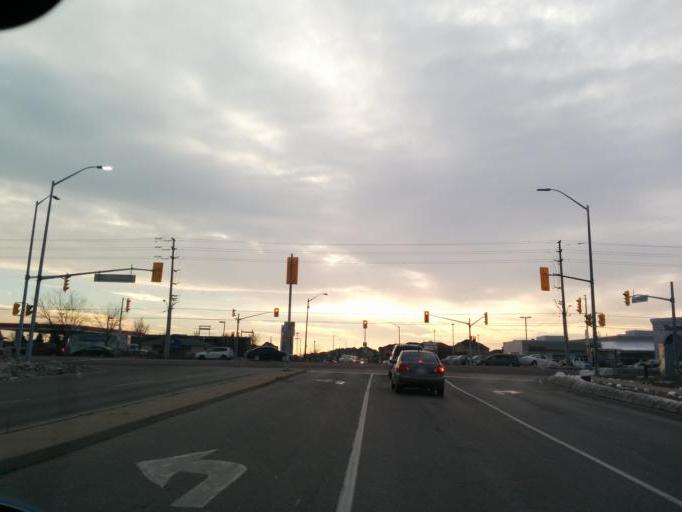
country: CA
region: Ontario
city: Mississauga
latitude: 43.6176
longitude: -79.7020
